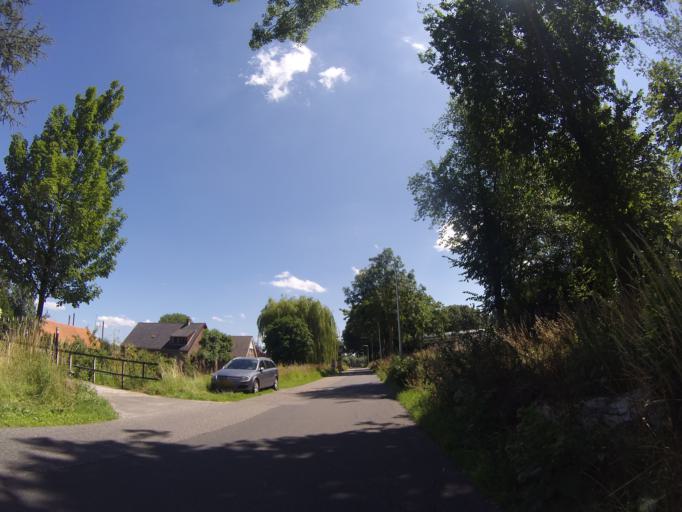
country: NL
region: Utrecht
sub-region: Gemeente Utrecht
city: Utrecht
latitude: 52.1213
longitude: 5.1210
